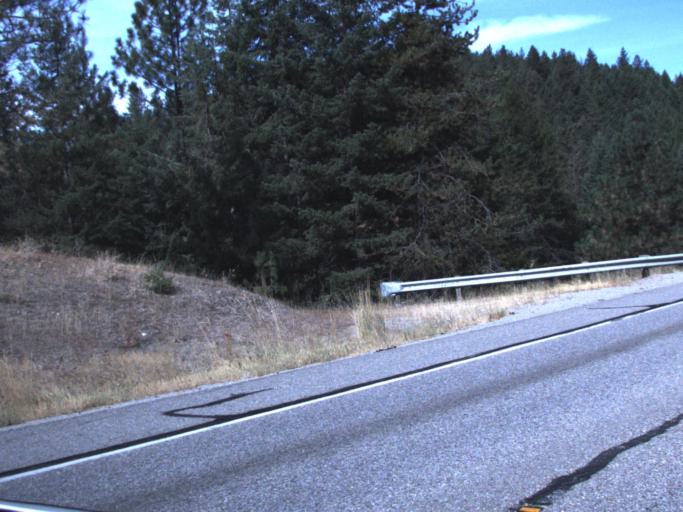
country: US
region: Washington
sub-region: Stevens County
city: Chewelah
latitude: 48.1363
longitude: -117.6564
